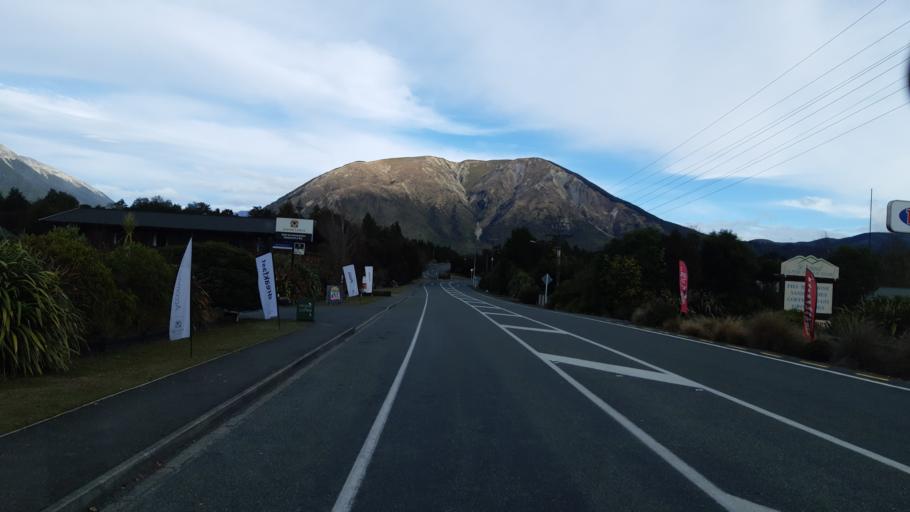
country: NZ
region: Tasman
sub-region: Tasman District
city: Wakefield
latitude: -41.8016
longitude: 172.8474
